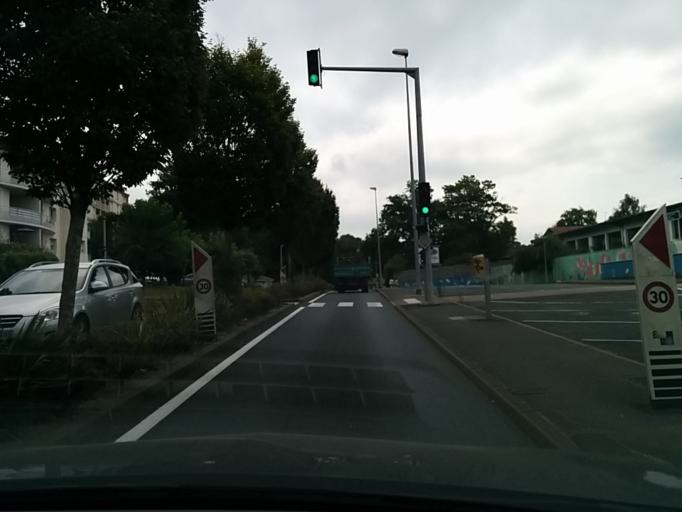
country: FR
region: Aquitaine
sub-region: Departement des Pyrenees-Atlantiques
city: Anglet
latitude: 43.4799
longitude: -1.5071
